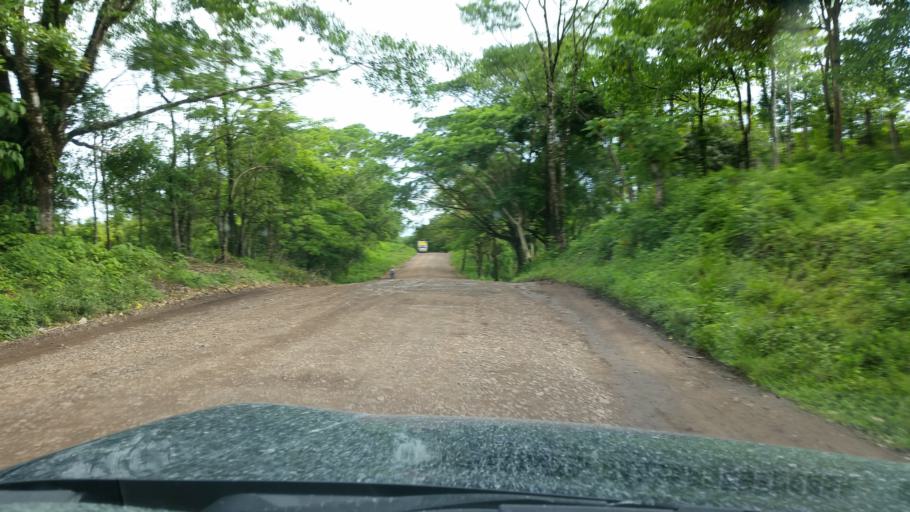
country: NI
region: Atlantico Norte (RAAN)
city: Siuna
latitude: 13.4475
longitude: -84.8563
